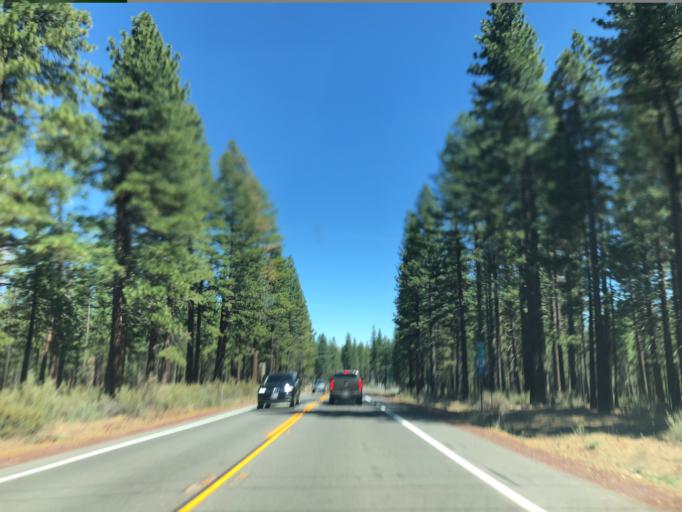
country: US
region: California
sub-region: Lassen County
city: Susanville
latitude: 40.4130
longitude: -120.7583
